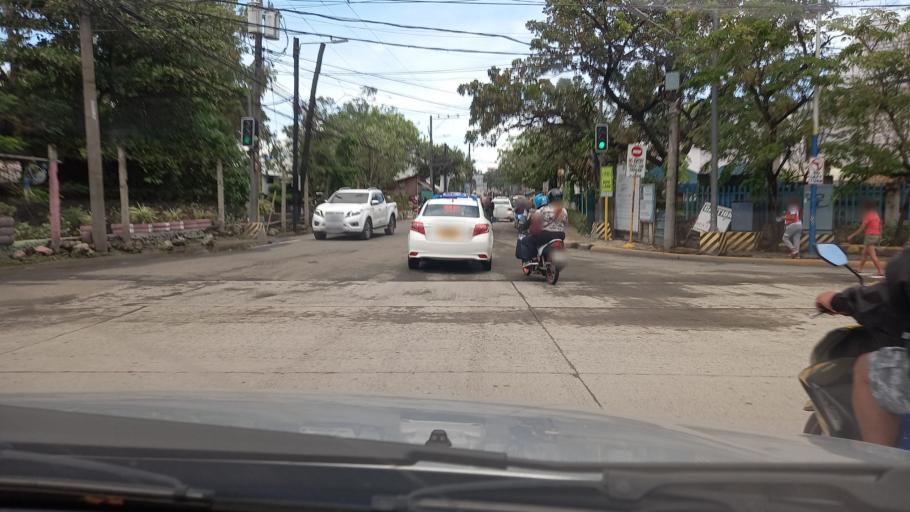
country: PH
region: Central Visayas
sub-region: Lapu-Lapu City
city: Buagsong
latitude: 10.3246
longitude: 123.9414
